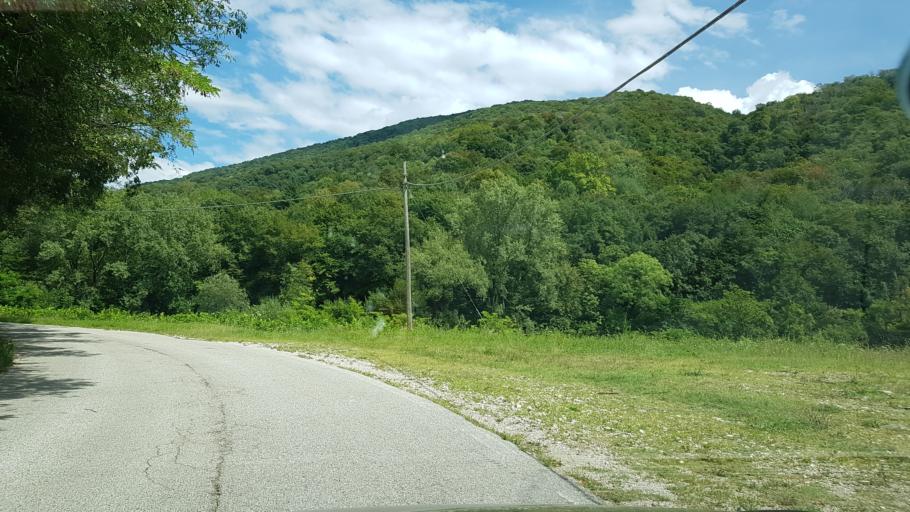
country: IT
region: Friuli Venezia Giulia
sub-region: Provincia di Udine
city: San Leonardo
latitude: 46.0675
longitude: 13.5287
